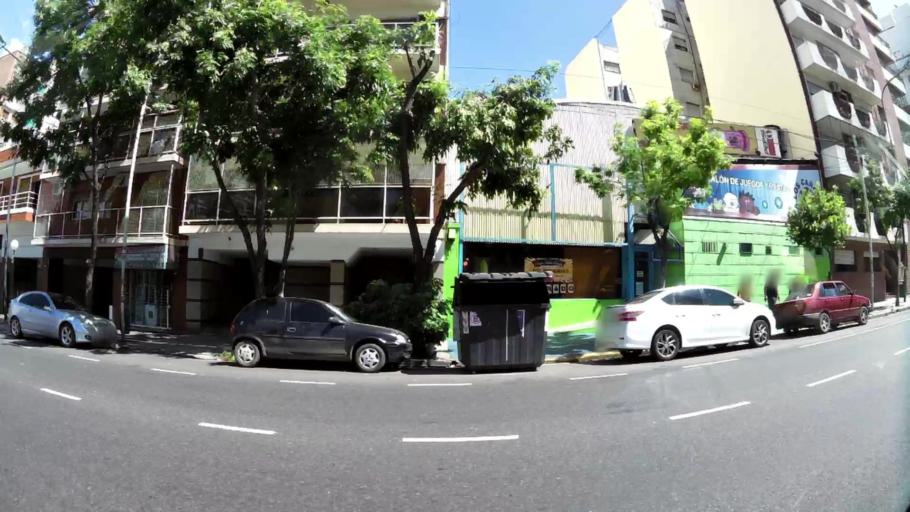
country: AR
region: Buenos Aires F.D.
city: Villa Santa Rita
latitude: -34.6231
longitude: -58.4416
